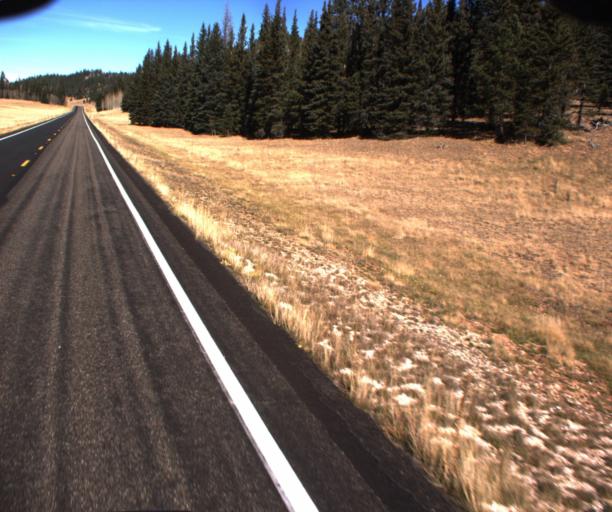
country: US
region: Arizona
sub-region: Coconino County
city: Grand Canyon
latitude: 36.4645
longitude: -112.1272
